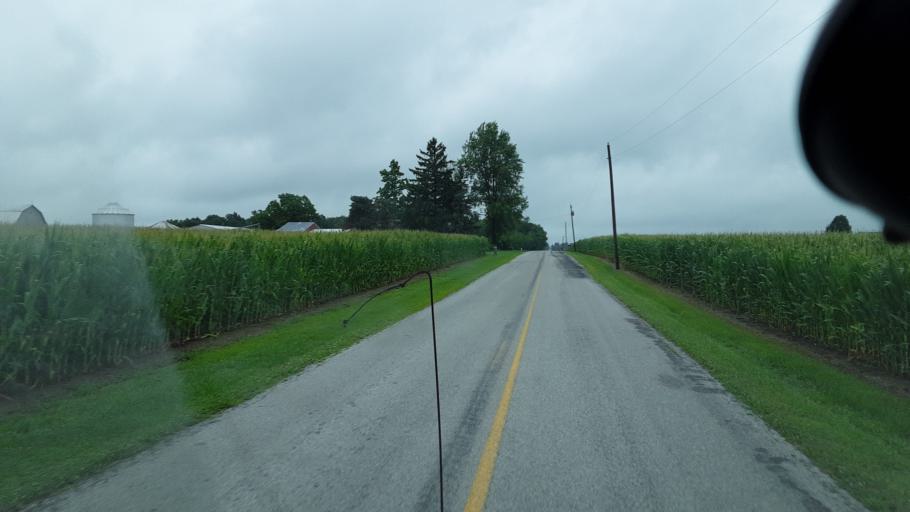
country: US
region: Indiana
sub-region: Wells County
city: Ossian
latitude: 40.9127
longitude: -85.1097
